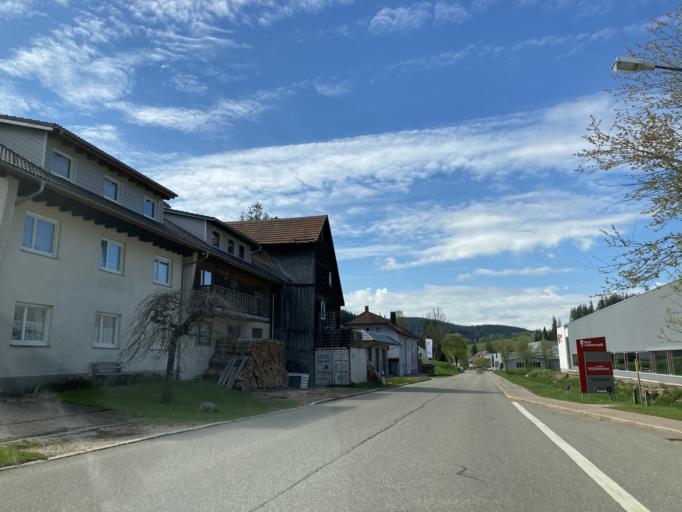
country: DE
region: Baden-Wuerttemberg
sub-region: Freiburg Region
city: Furtwangen im Schwarzwald
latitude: 48.0635
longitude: 8.2057
